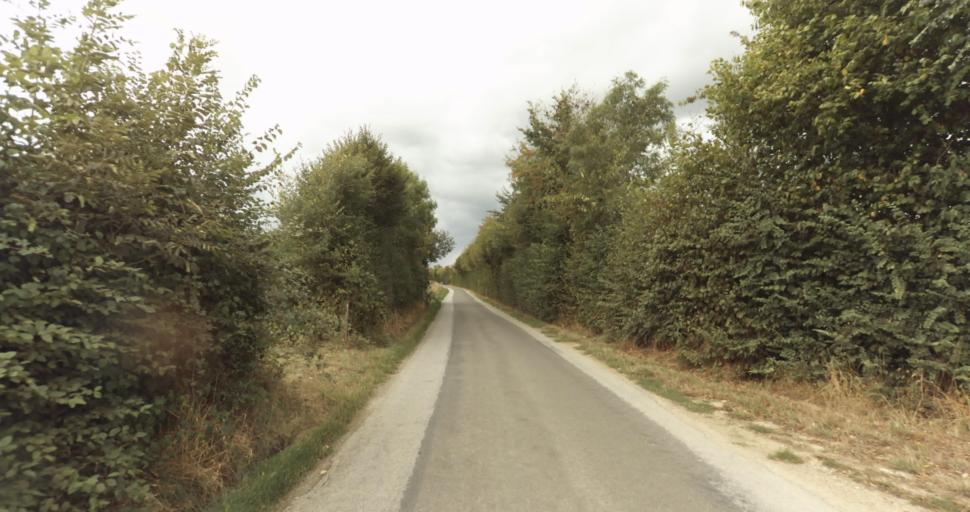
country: FR
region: Lower Normandy
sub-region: Departement de l'Orne
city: Gace
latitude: 48.9038
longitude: 0.3489
